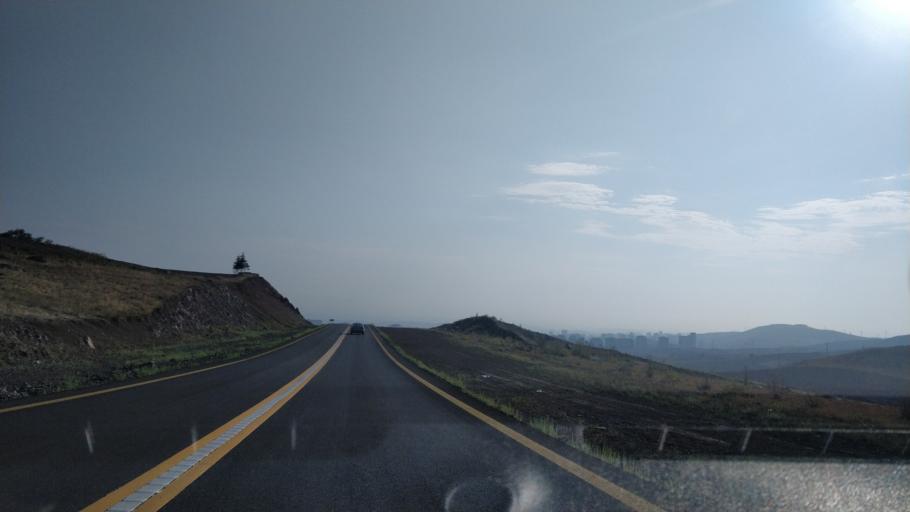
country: TR
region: Ankara
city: Etimesgut
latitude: 39.8739
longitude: 32.5960
